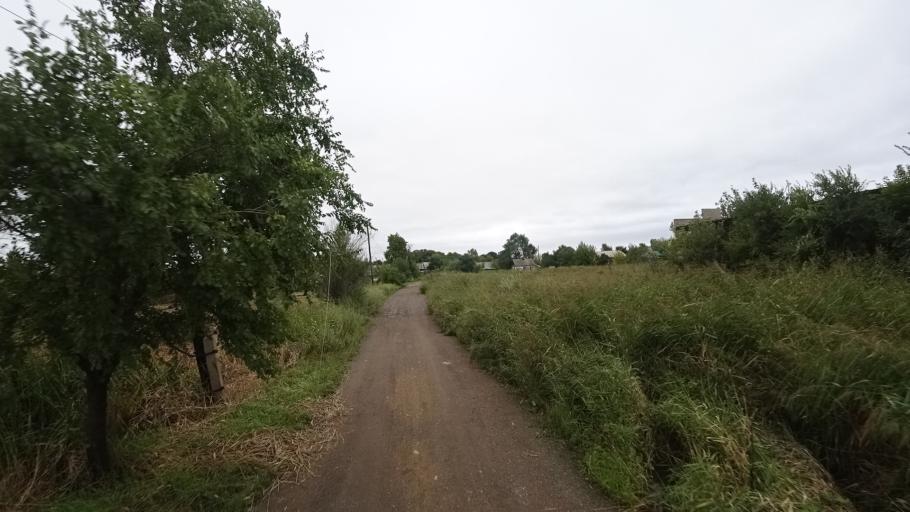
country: RU
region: Primorskiy
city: Chernigovka
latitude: 44.3369
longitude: 132.5428
